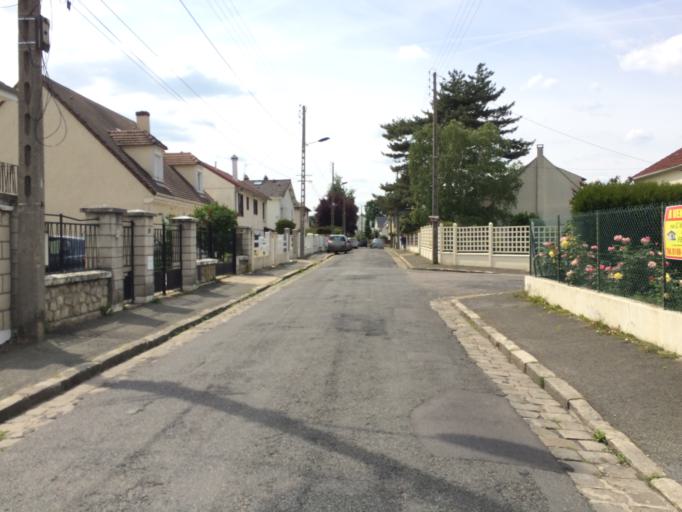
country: FR
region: Ile-de-France
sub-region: Departement de l'Essonne
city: Vauhallan
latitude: 48.7257
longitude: 2.2202
